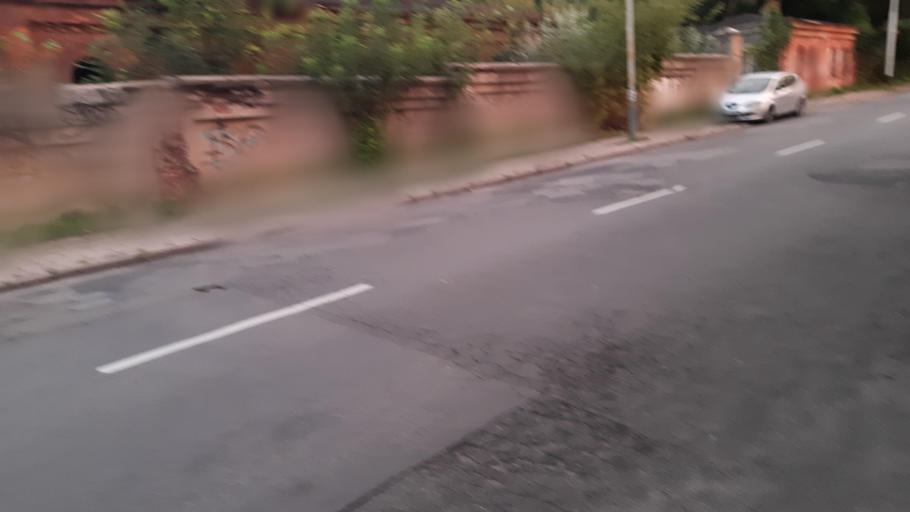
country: PL
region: Lodz Voivodeship
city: Lodz
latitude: 51.7569
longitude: 19.4778
